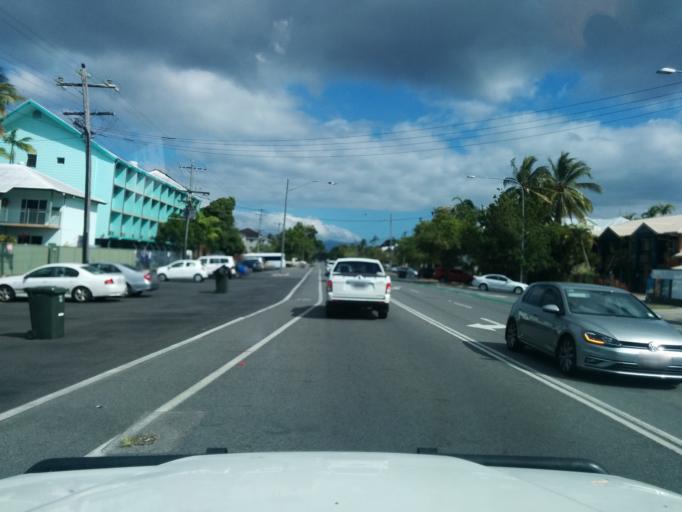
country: AU
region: Queensland
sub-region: Cairns
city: Cairns
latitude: -16.9093
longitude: 145.7603
